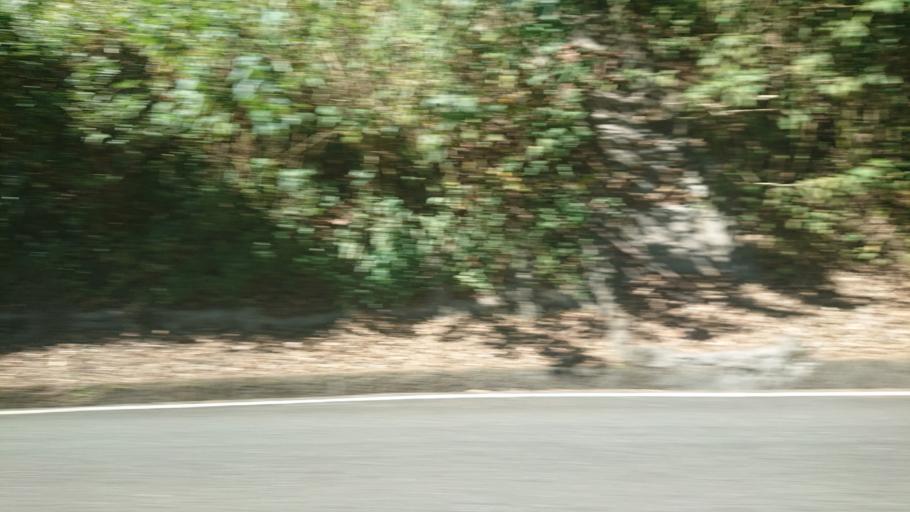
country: TW
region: Taiwan
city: Lugu
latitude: 23.4876
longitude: 120.7523
